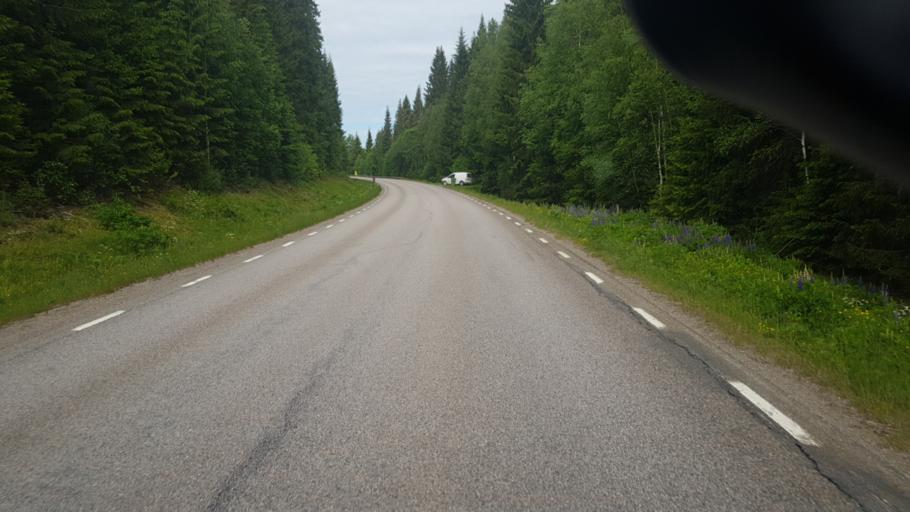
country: SE
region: Vaermland
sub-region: Eda Kommun
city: Charlottenberg
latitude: 59.8832
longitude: 12.3675
